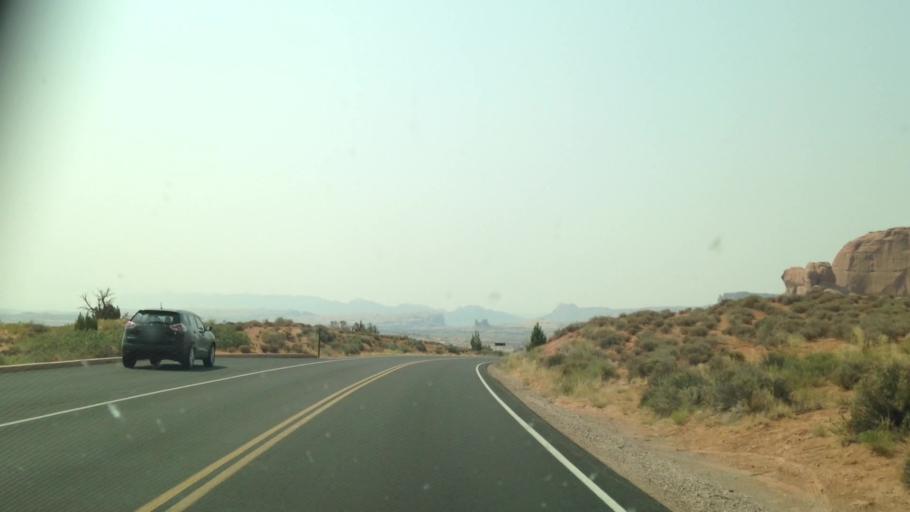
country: US
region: Utah
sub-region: Grand County
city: Moab
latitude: 38.6657
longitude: -109.5876
